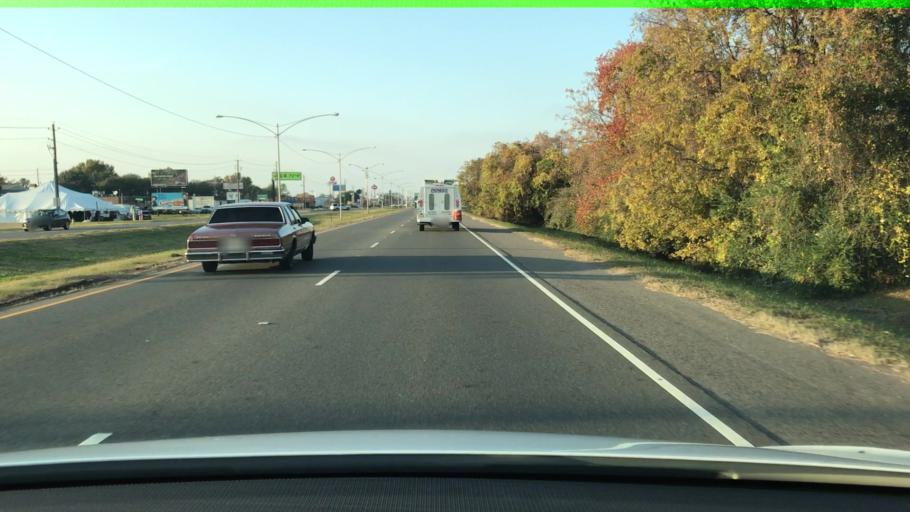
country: US
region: Louisiana
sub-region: Bossier Parish
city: Bossier City
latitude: 32.4220
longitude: -93.7060
